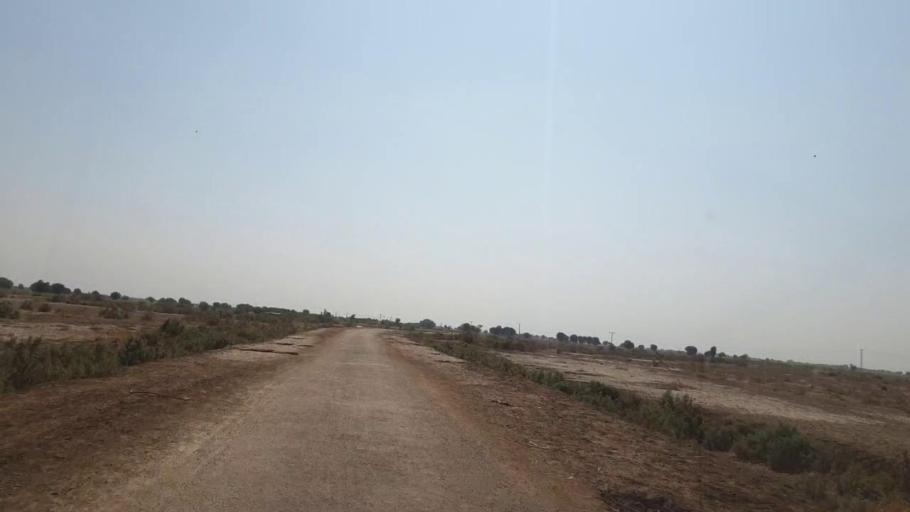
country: PK
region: Sindh
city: Kunri
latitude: 25.0849
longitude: 69.4738
